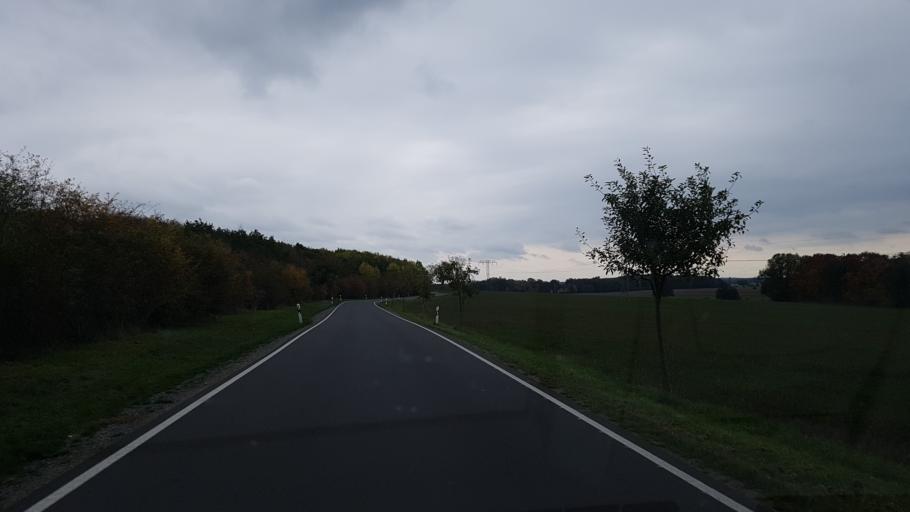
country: DE
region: Saxony
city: Falkenhain
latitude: 51.3864
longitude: 12.8986
